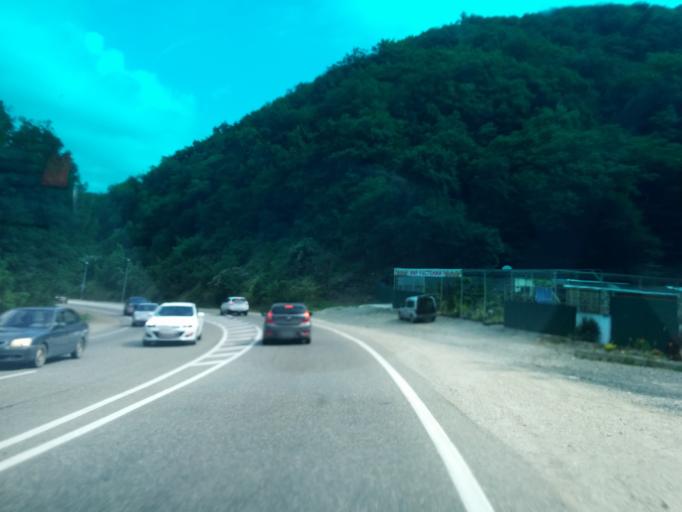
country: RU
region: Krasnodarskiy
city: Nebug
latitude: 44.1755
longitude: 38.9771
